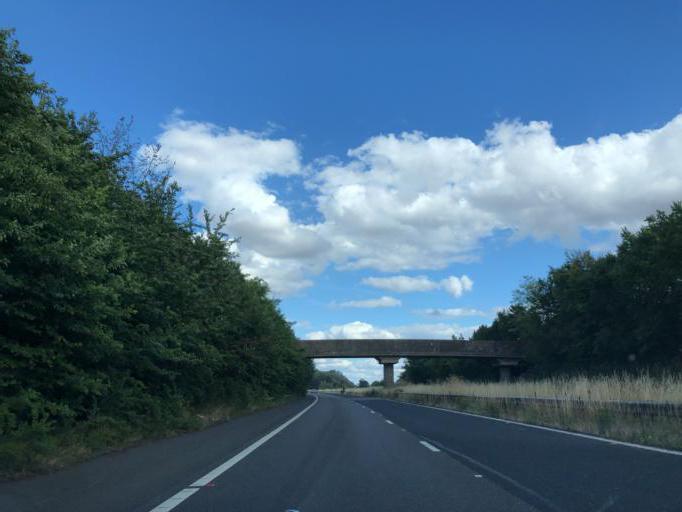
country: GB
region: England
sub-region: Northamptonshire
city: Daventry
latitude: 52.3280
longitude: -1.1659
